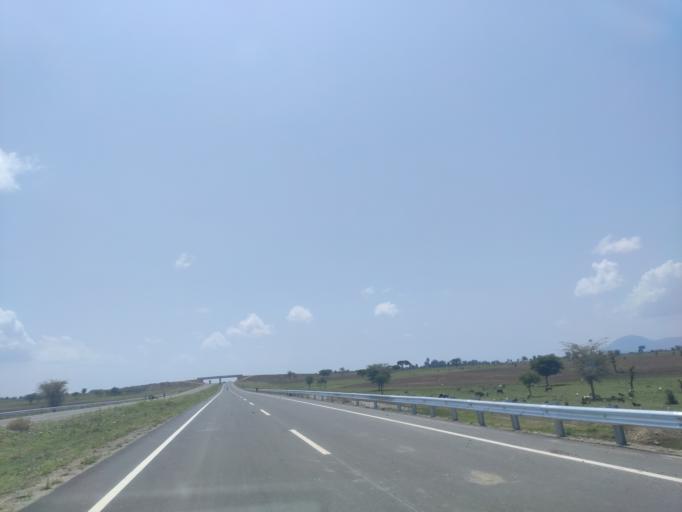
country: ET
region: Oromiya
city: Ziway
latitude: 8.2396
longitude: 38.8801
